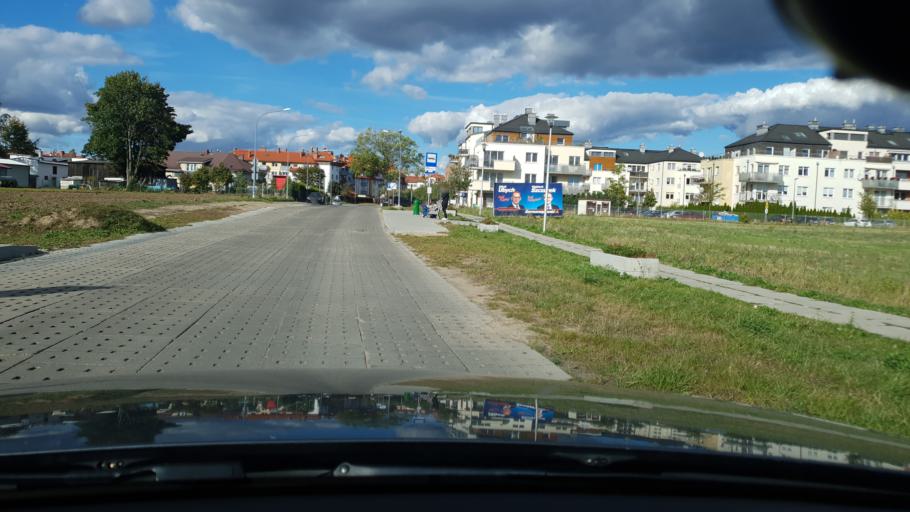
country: PL
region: Pomeranian Voivodeship
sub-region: Powiat kartuski
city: Chwaszczyno
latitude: 54.4931
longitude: 18.4364
